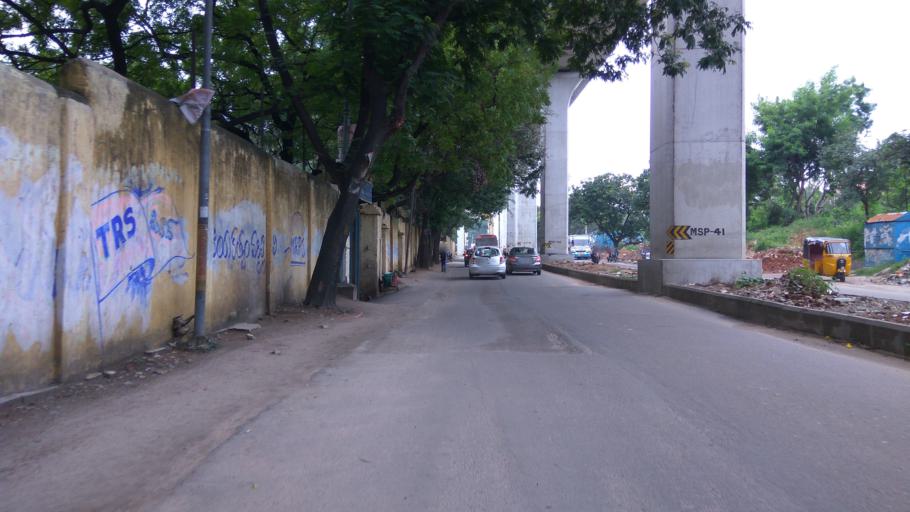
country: IN
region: Telangana
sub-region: Hyderabad
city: Malkajgiri
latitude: 17.4333
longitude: 78.5089
